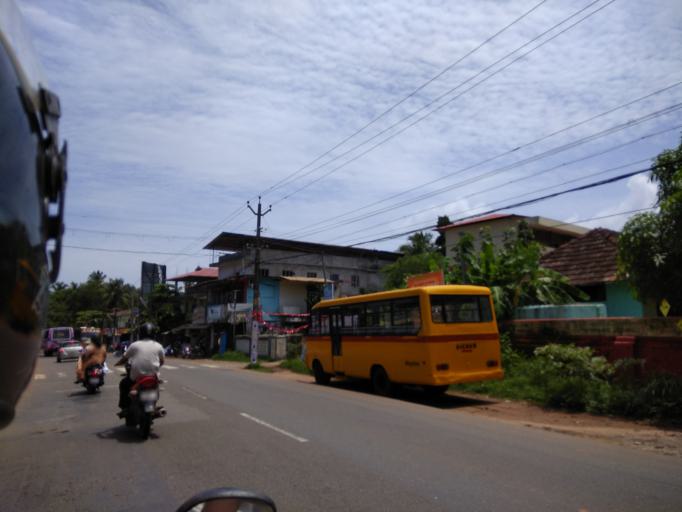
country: IN
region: Kerala
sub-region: Thrissur District
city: Trichur
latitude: 10.4977
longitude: 76.1473
